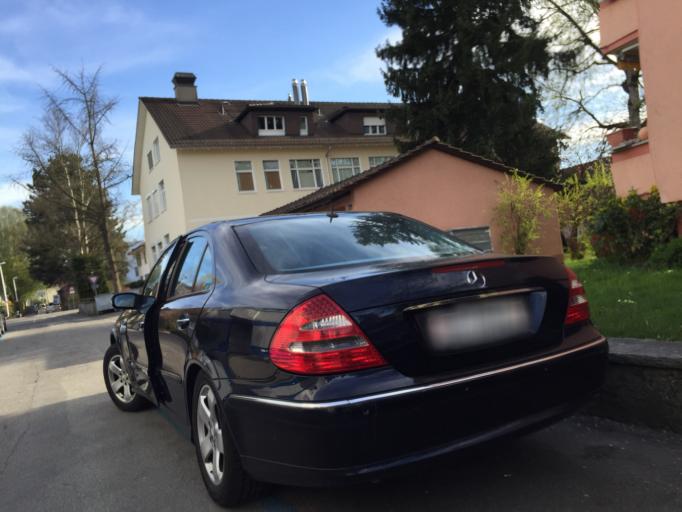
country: CH
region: Bern
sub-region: Bern-Mittelland District
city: Koniz
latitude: 46.9335
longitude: 7.4170
